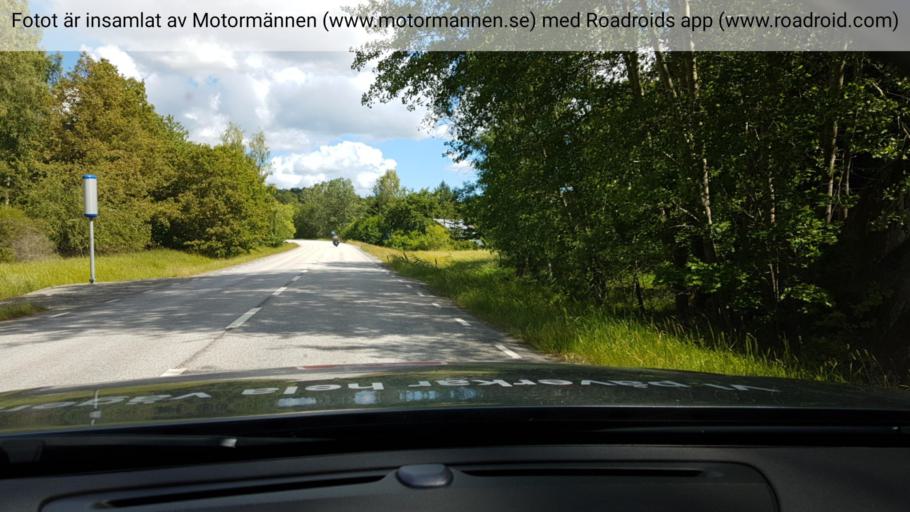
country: SE
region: Stockholm
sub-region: Varmdo Kommun
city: Hemmesta
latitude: 59.3601
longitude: 18.5133
